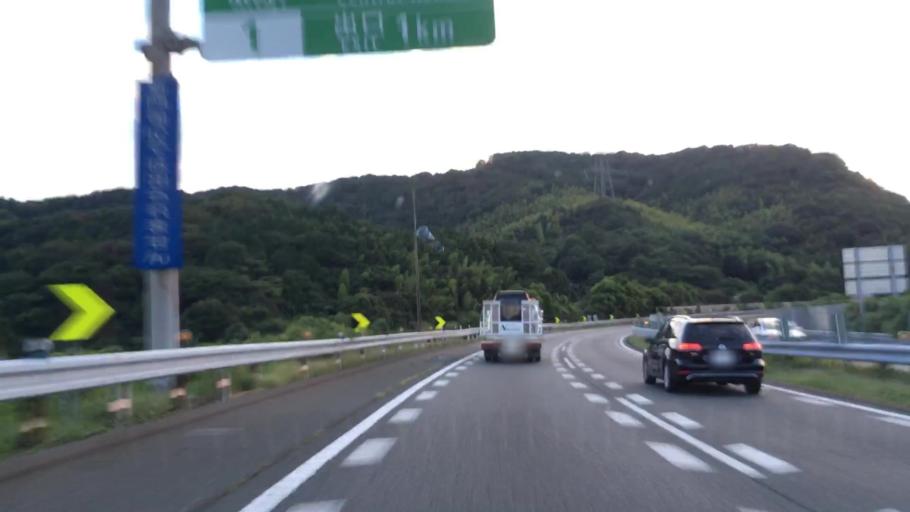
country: JP
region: Yamaguchi
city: Shimonoseki
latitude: 33.9284
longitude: 130.9930
